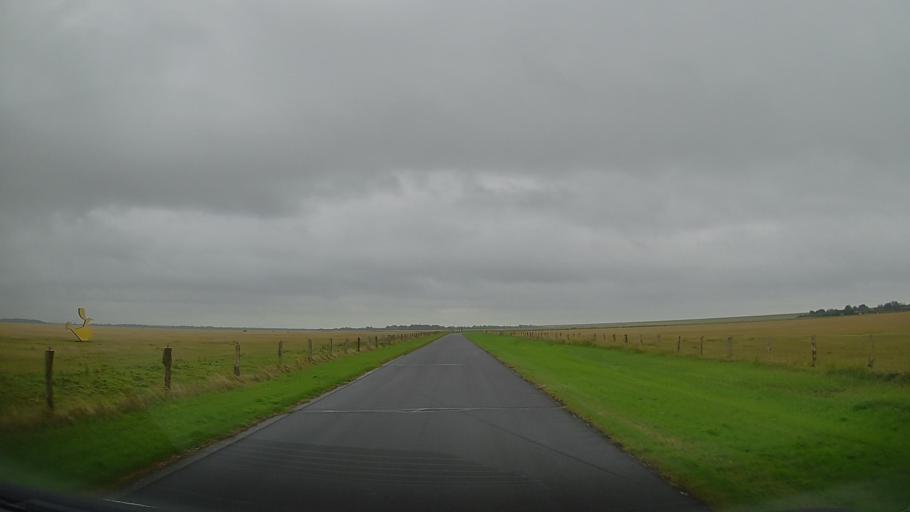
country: DE
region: Schleswig-Holstein
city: Friedrichsgabekoog
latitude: 54.1152
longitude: 8.9519
